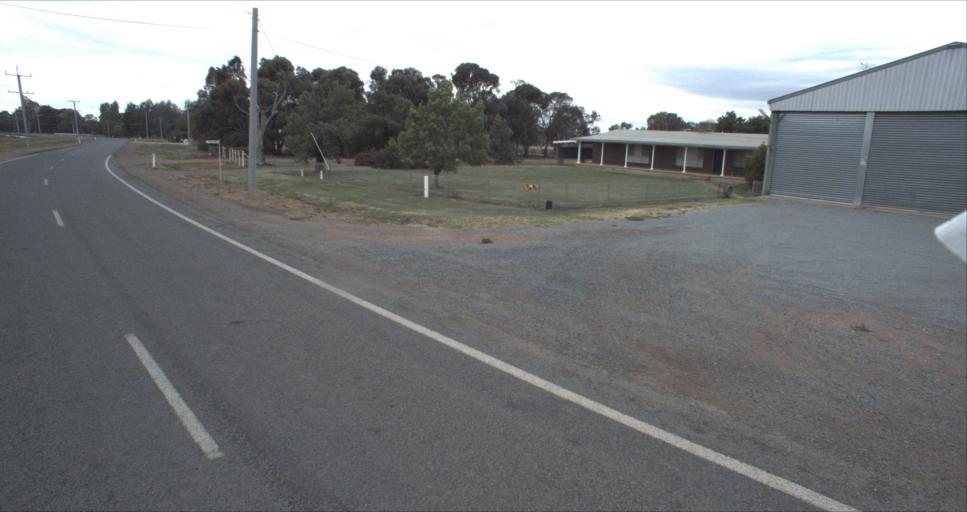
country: AU
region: New South Wales
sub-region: Leeton
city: Leeton
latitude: -34.5388
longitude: 146.3873
